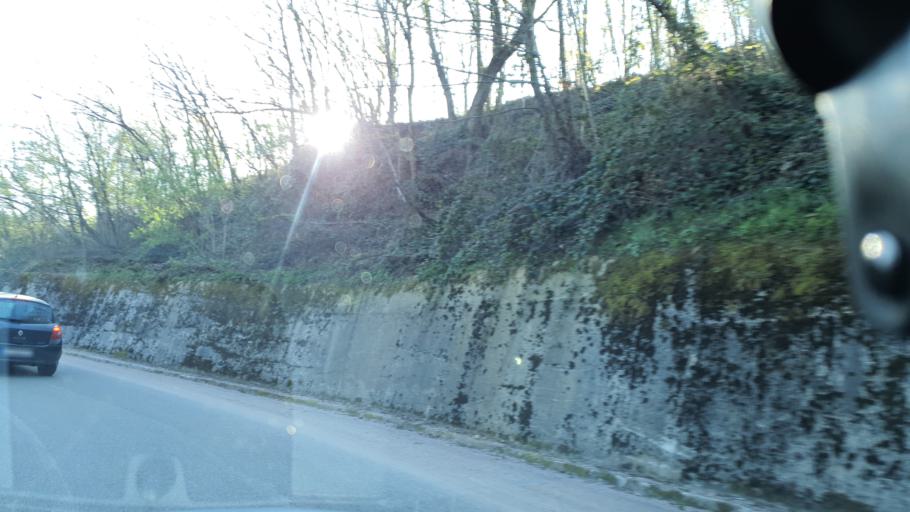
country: RS
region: Central Serbia
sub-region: Kolubarski Okrug
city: Osecina
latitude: 44.2769
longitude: 19.5232
